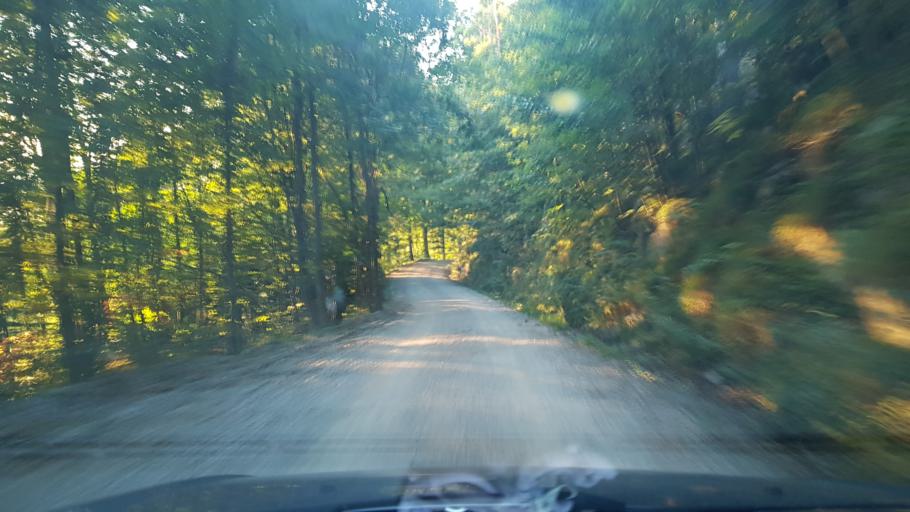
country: SI
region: Vipava
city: Vipava
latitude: 45.7819
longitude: 14.0407
